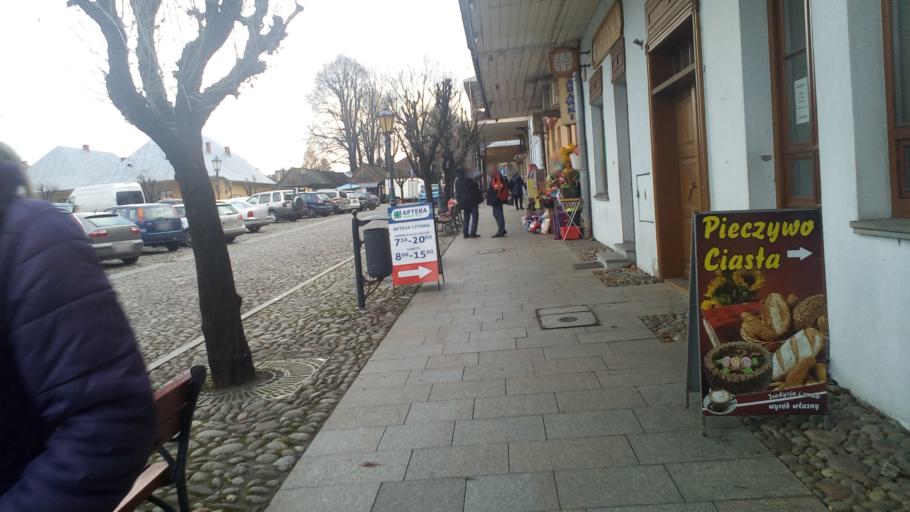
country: PL
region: Lesser Poland Voivodeship
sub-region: Powiat nowosadecki
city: Stary Sacz
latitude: 49.5638
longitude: 20.6349
